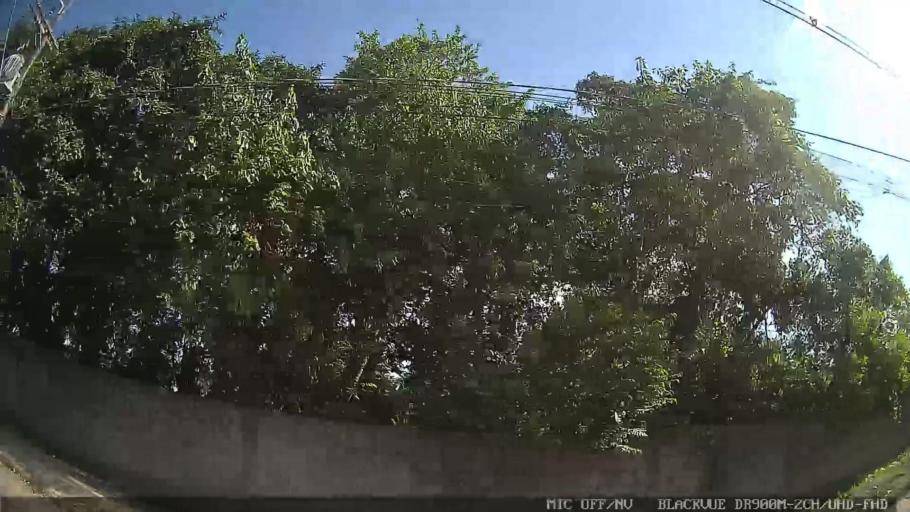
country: BR
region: Sao Paulo
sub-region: Guaruja
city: Guaruja
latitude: -23.9758
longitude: -46.2216
